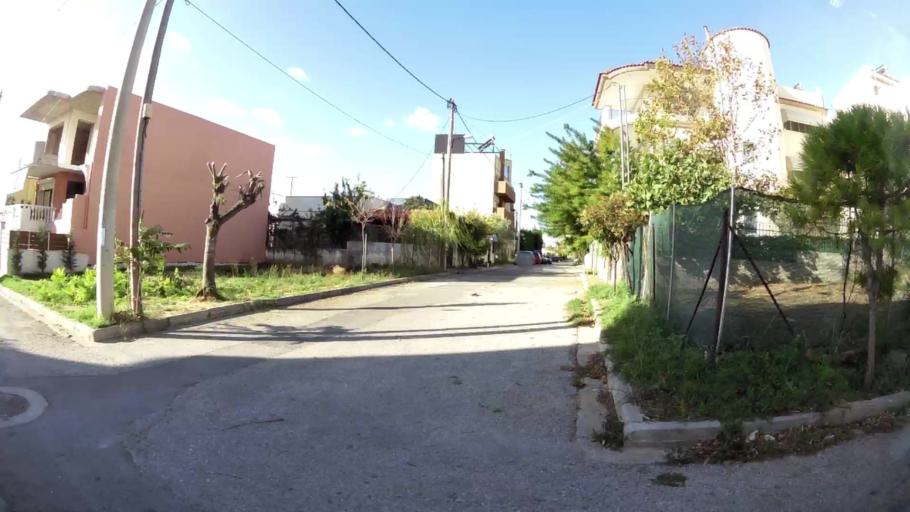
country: GR
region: Attica
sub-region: Nomarchia Anatolikis Attikis
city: Acharnes
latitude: 38.0704
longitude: 23.7453
